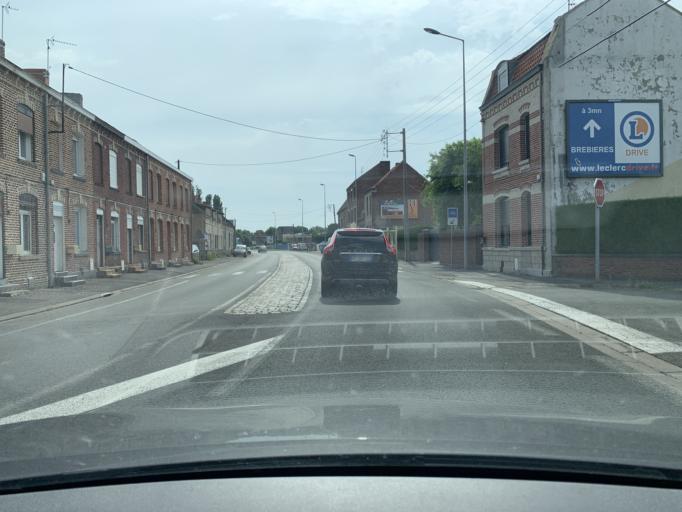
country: FR
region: Nord-Pas-de-Calais
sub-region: Departement du Nord
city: Douai
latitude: 50.3609
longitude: 3.0595
